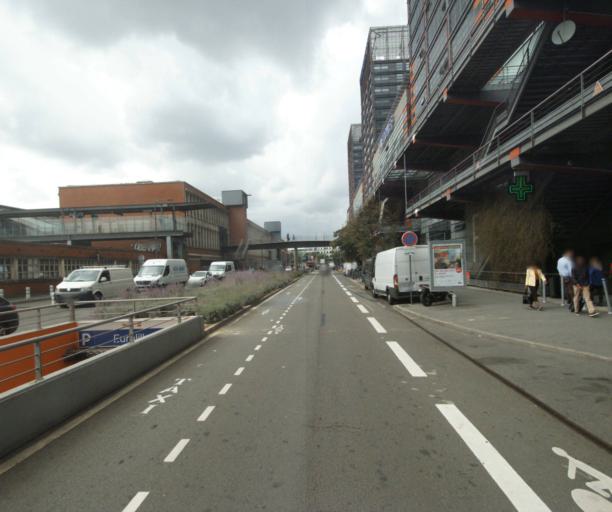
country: FR
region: Nord-Pas-de-Calais
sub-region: Departement du Nord
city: La Madeleine
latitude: 50.6365
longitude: 3.0746
